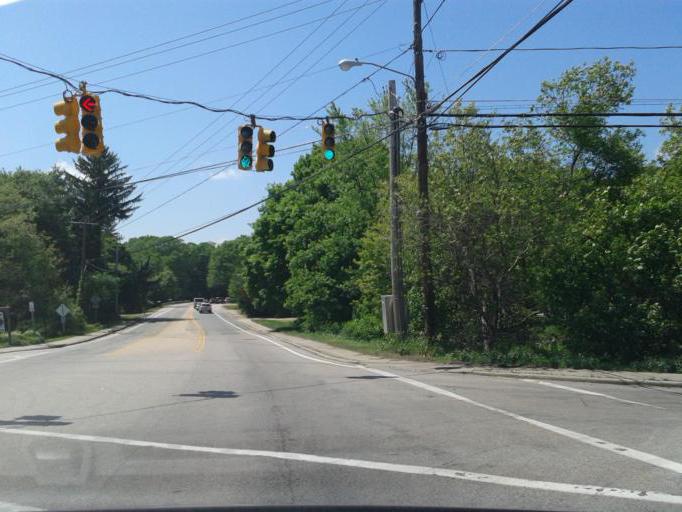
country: US
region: Rhode Island
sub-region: Washington County
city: Kingston
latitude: 41.4851
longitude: -71.5612
